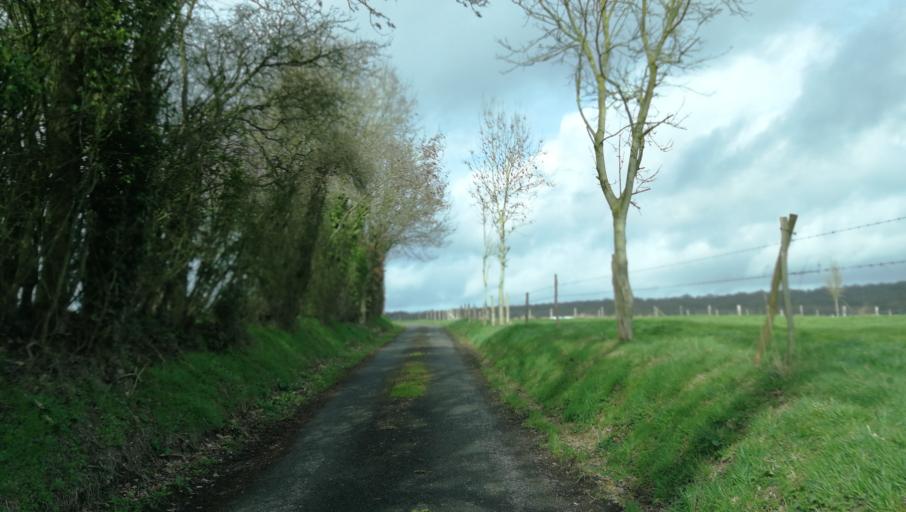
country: FR
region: Haute-Normandie
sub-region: Departement de l'Eure
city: Lieurey
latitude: 49.2308
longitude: 0.5412
